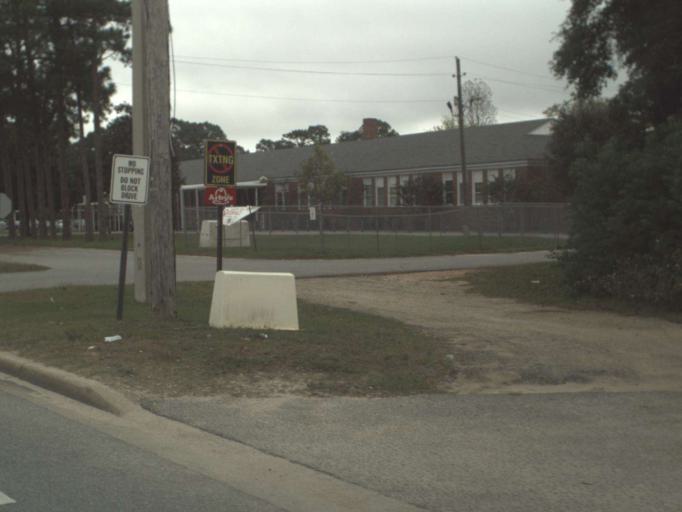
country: US
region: Florida
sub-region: Escambia County
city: Brent
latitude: 30.4616
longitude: -87.2403
